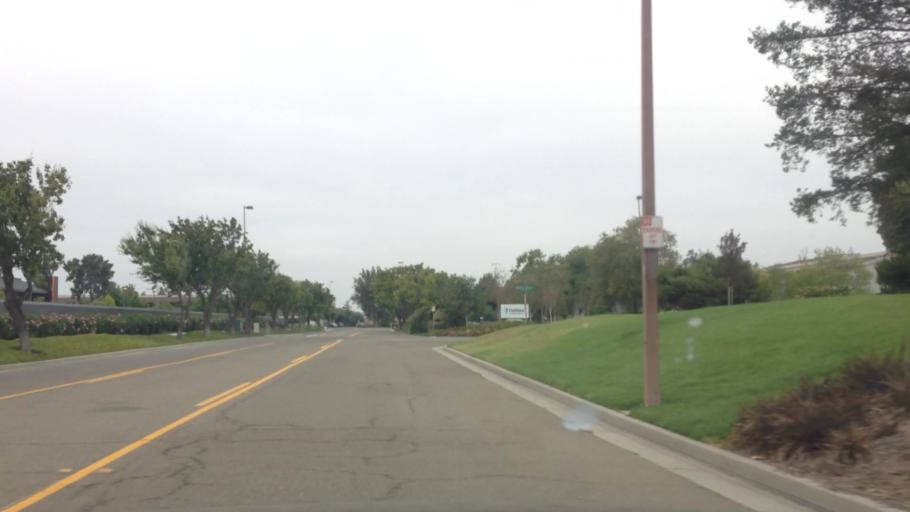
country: US
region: California
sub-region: Santa Clara County
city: Santa Clara
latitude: 37.4057
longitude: -121.9813
